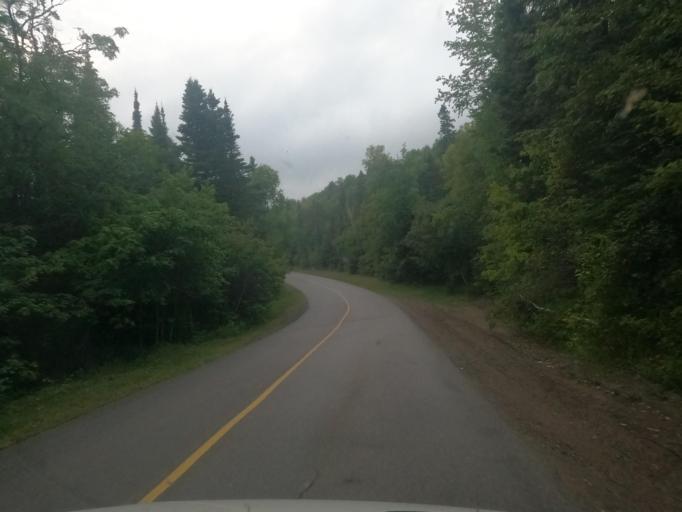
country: CA
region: Ontario
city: Marathon
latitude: 48.7787
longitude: -87.1057
